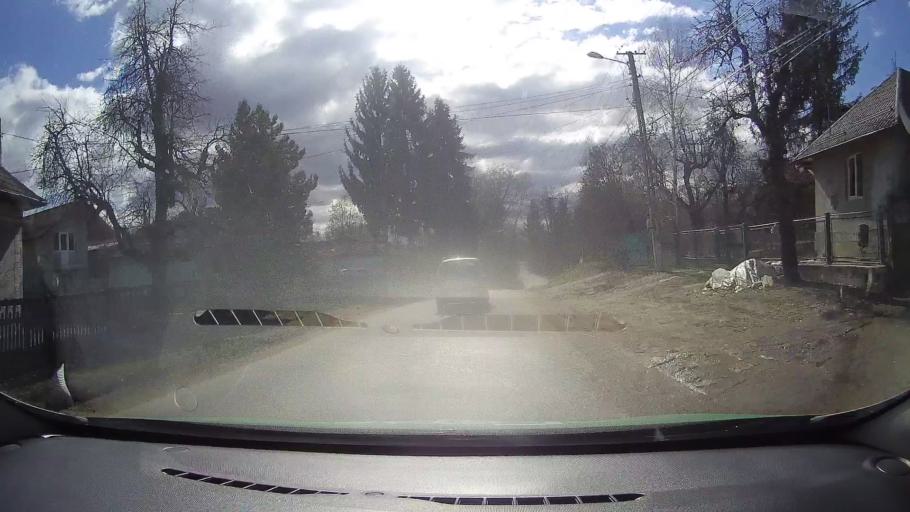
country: RO
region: Dambovita
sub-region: Oras Pucioasa
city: Pucioasa
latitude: 45.0615
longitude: 25.4252
